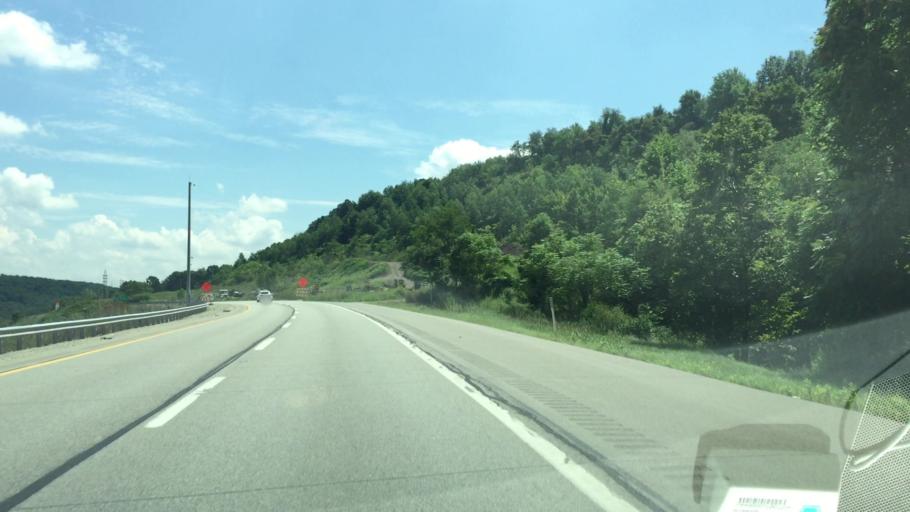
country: US
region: Pennsylvania
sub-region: Allegheny County
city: Ben Avon
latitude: 40.5394
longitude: -80.0803
